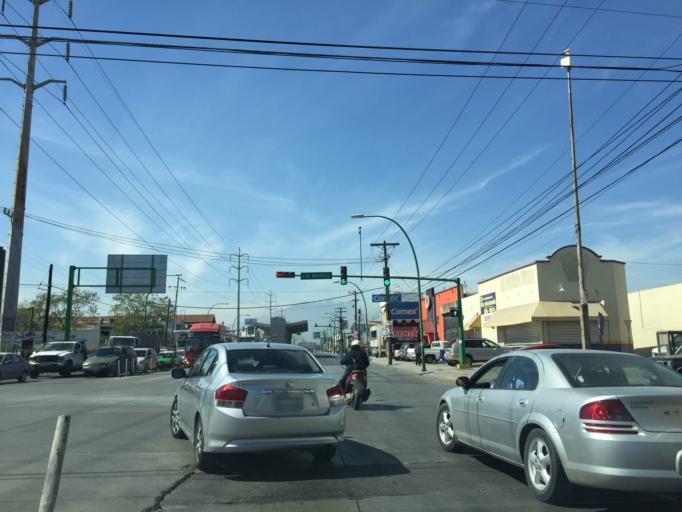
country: MX
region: Nuevo Leon
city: Guadalupe
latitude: 25.7031
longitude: -100.2465
